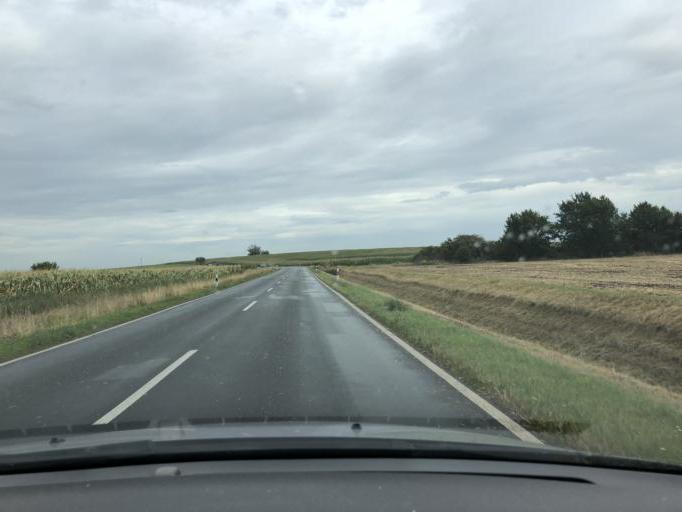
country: DE
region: Saxony-Anhalt
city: Gross Rosenburg
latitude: 51.8570
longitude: 11.8583
